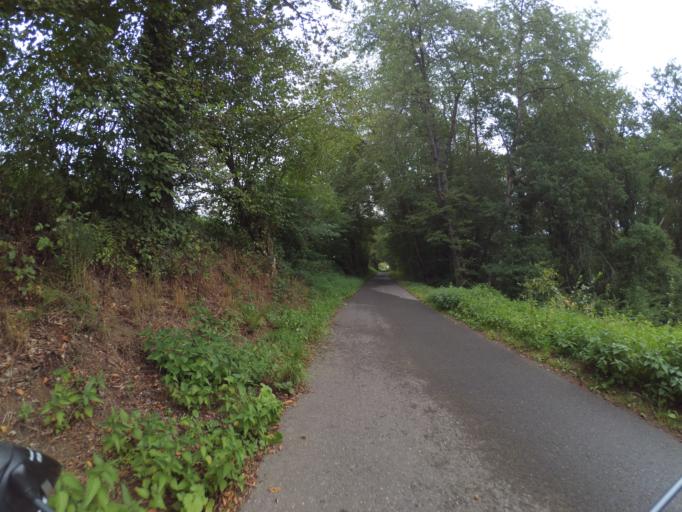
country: DE
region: Rheinland-Pfalz
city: Beilingen
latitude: 49.9545
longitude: 6.6781
